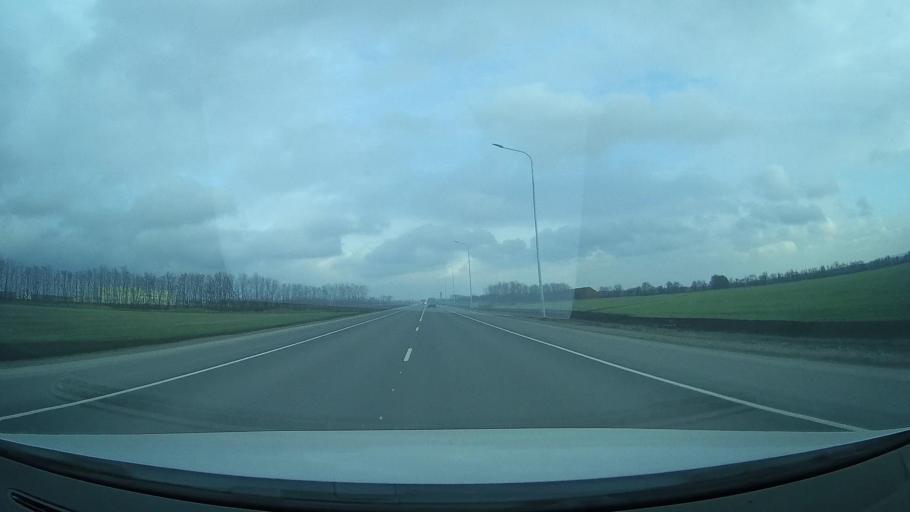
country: RU
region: Rostov
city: Grushevskaya
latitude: 47.4716
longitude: 39.9059
